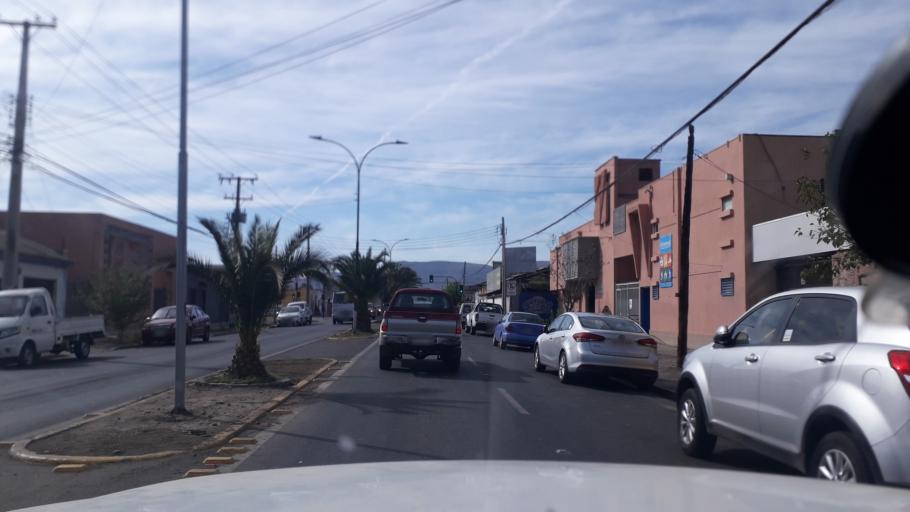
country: CL
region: Valparaiso
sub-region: Provincia de San Felipe
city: San Felipe
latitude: -32.7509
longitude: -70.7304
